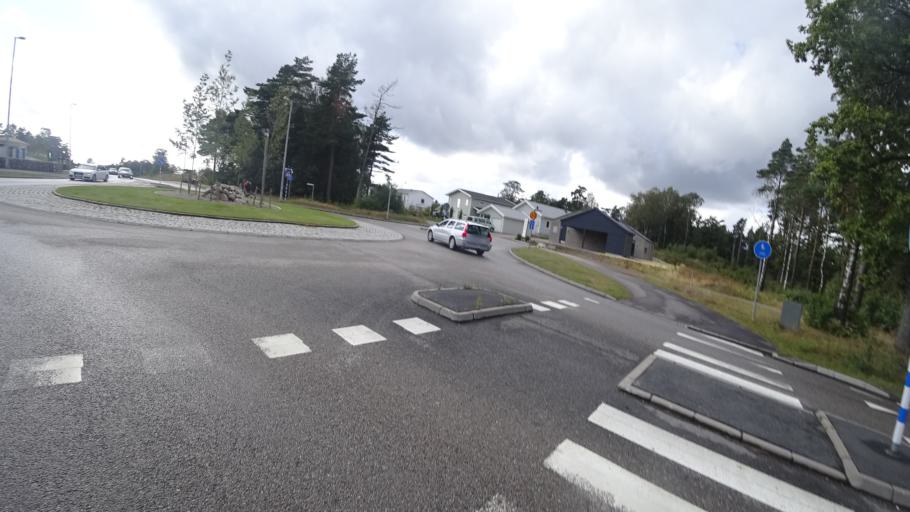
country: SE
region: Vaestra Goetaland
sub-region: Partille Kommun
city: Ojersjo
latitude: 57.6845
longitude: 12.1014
